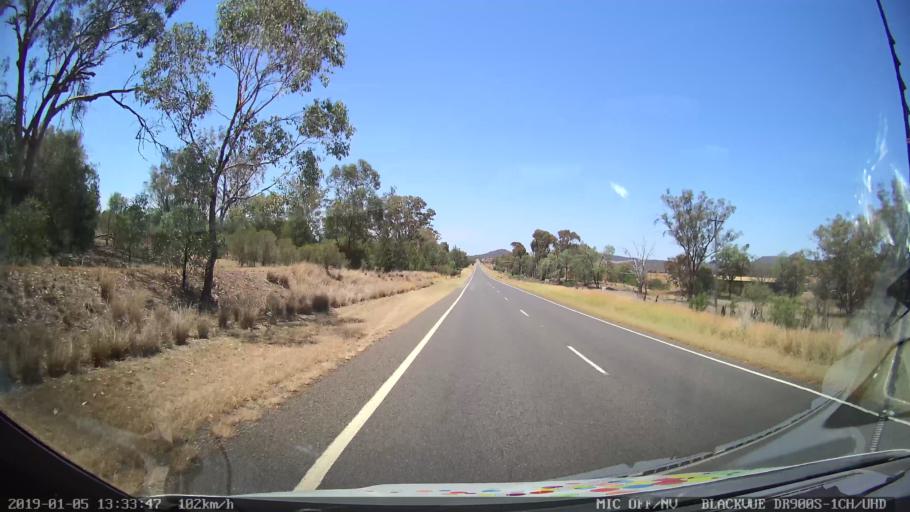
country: AU
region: New South Wales
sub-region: Gunnedah
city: Gunnedah
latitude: -30.9990
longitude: 150.1222
